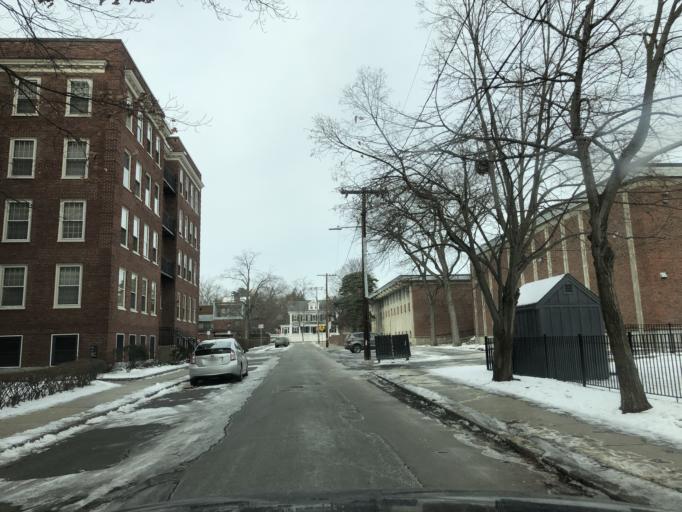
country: US
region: Massachusetts
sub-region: Middlesex County
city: Cambridge
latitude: 42.3821
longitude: -71.1238
